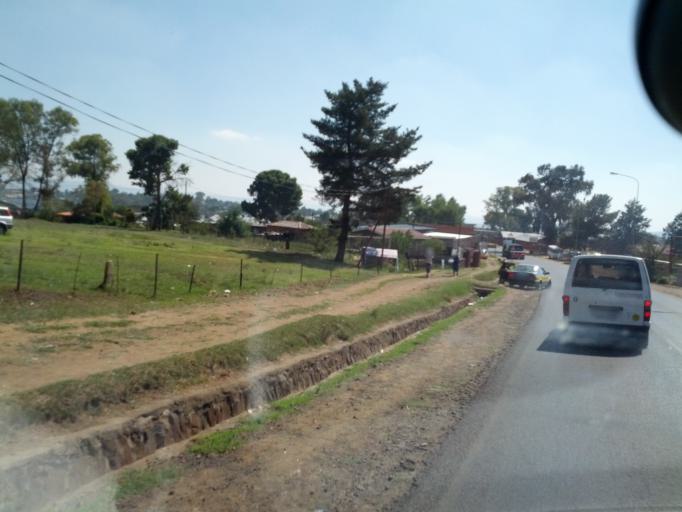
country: LS
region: Berea
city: Teyateyaneng
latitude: -29.1522
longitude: 27.7446
